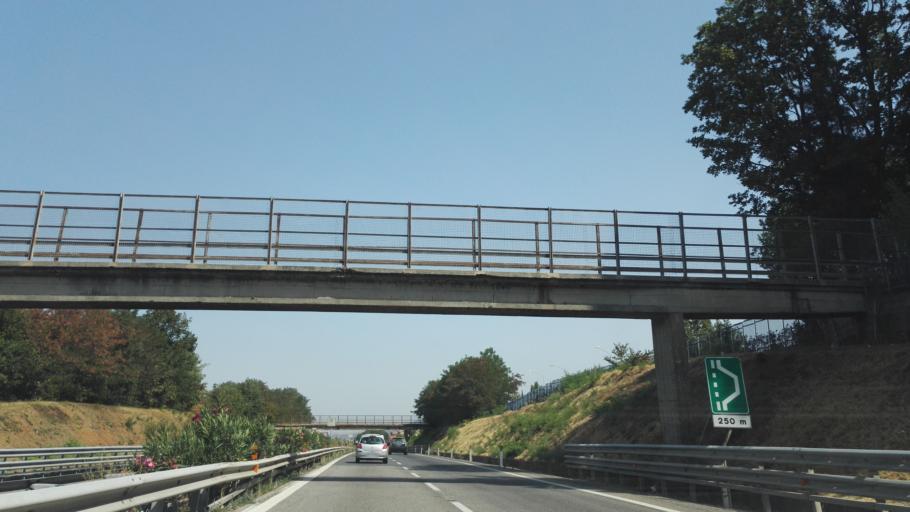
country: IT
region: Calabria
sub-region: Provincia di Cosenza
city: Piane Crati
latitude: 39.2221
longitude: 16.3045
